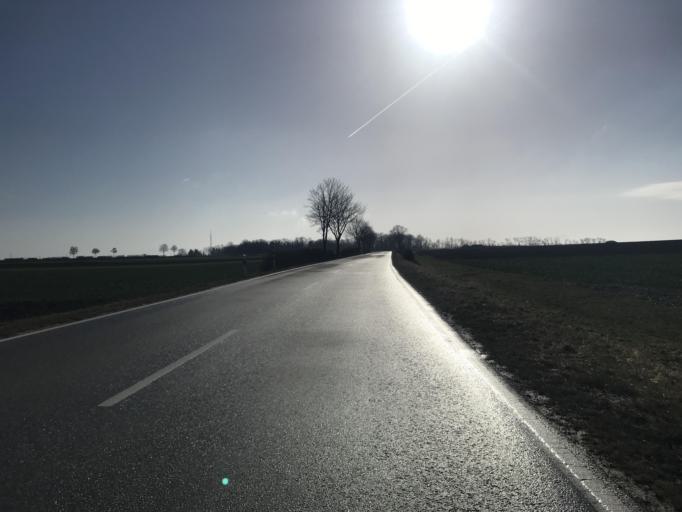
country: DE
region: Rheinland-Pfalz
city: Ober-Hilbersheim
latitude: 49.8869
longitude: 8.0239
